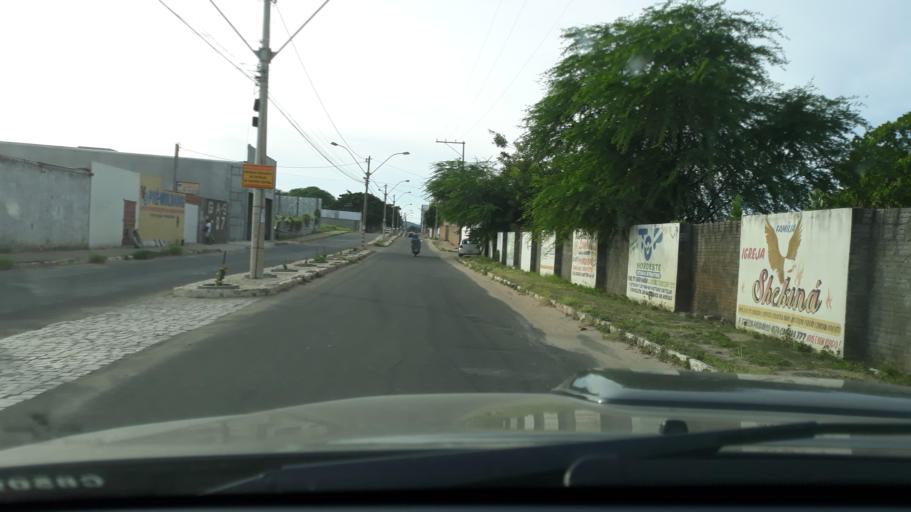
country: BR
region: Bahia
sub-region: Guanambi
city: Guanambi
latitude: -14.2346
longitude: -42.7732
